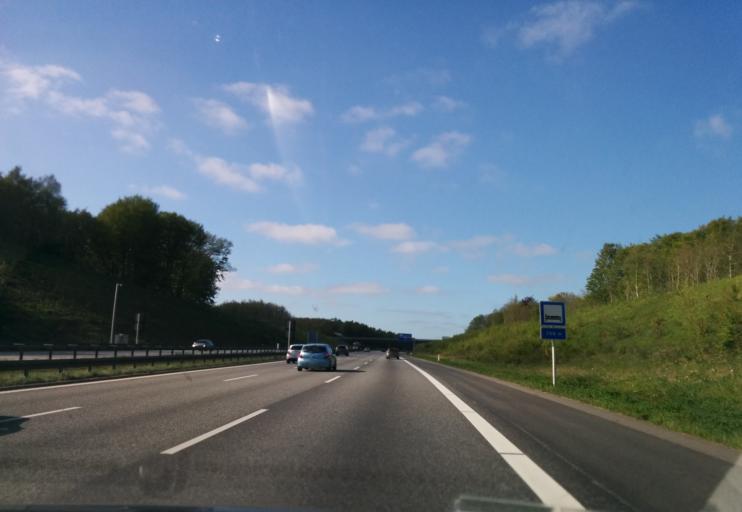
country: DK
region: South Denmark
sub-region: Vejle Kommune
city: Vejle
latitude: 55.7128
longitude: 9.5769
